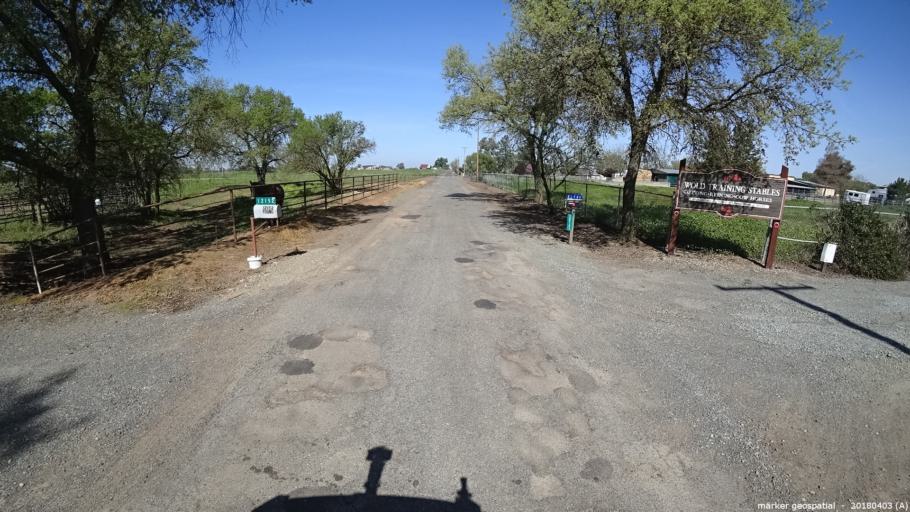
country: US
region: California
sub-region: Sacramento County
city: Wilton
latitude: 38.4291
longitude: -121.2212
